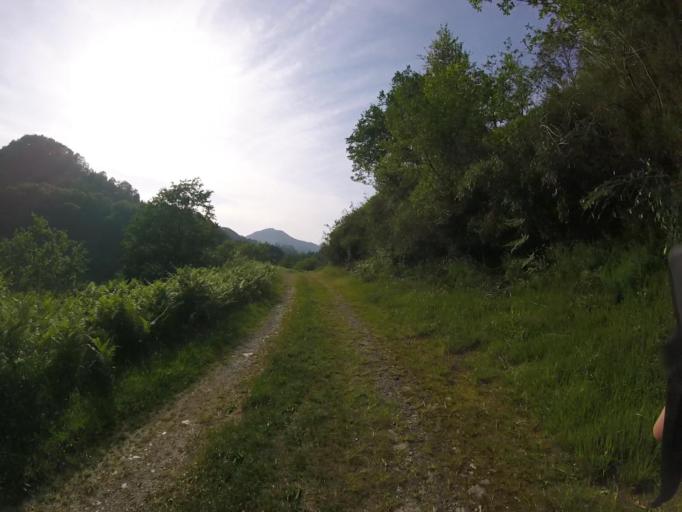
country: ES
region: Navarre
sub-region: Provincia de Navarra
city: Arano
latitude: 43.2228
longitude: -1.8641
